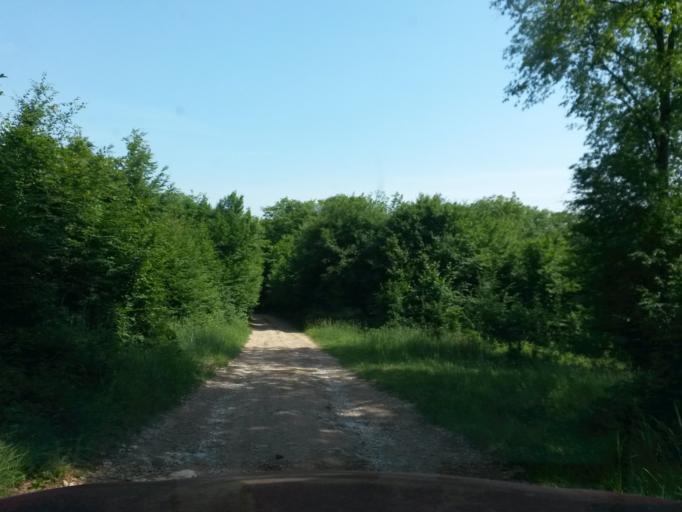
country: SK
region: Kosicky
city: Moldava nad Bodvou
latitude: 48.6429
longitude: 20.9543
